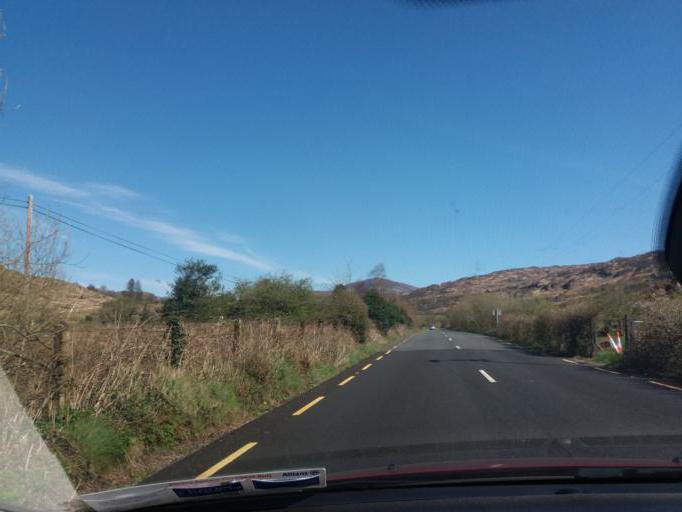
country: IE
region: Munster
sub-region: Ciarrai
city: Cill Airne
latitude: 51.9322
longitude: -9.3830
